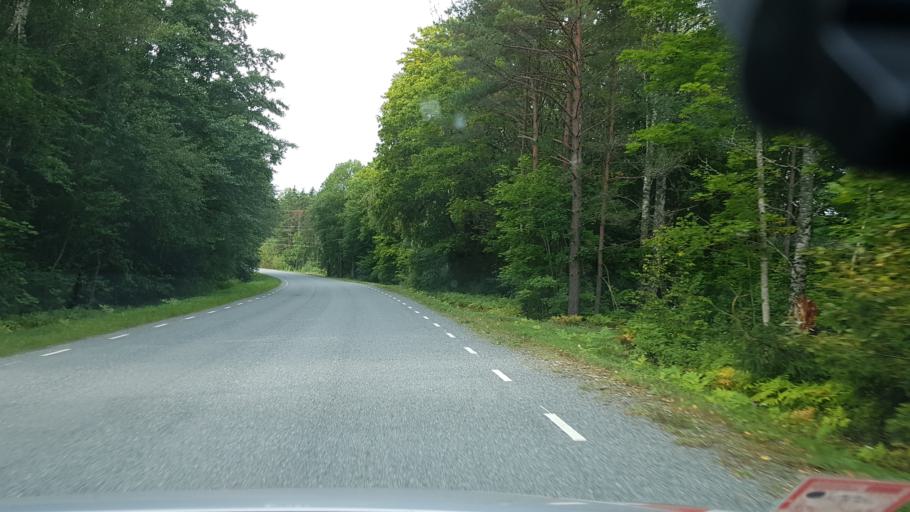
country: EE
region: Saare
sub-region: Kuressaare linn
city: Kuressaare
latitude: 58.4616
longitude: 22.7149
